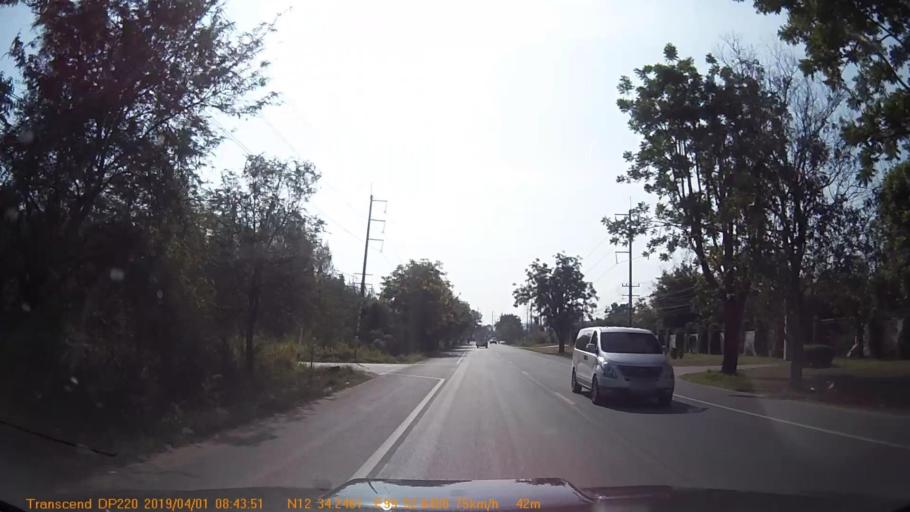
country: TH
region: Prachuap Khiri Khan
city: Hua Hin
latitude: 12.5706
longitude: 99.8813
